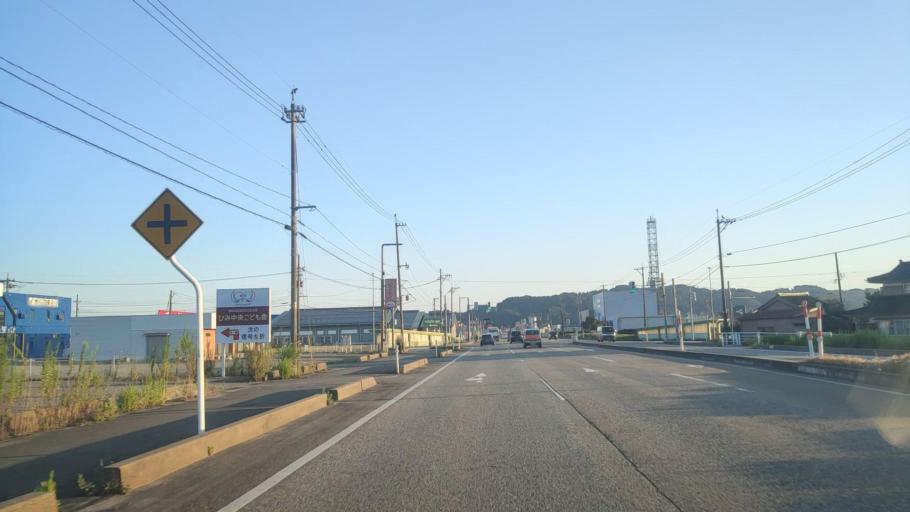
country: JP
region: Toyama
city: Himi
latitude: 36.8686
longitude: 136.9754
